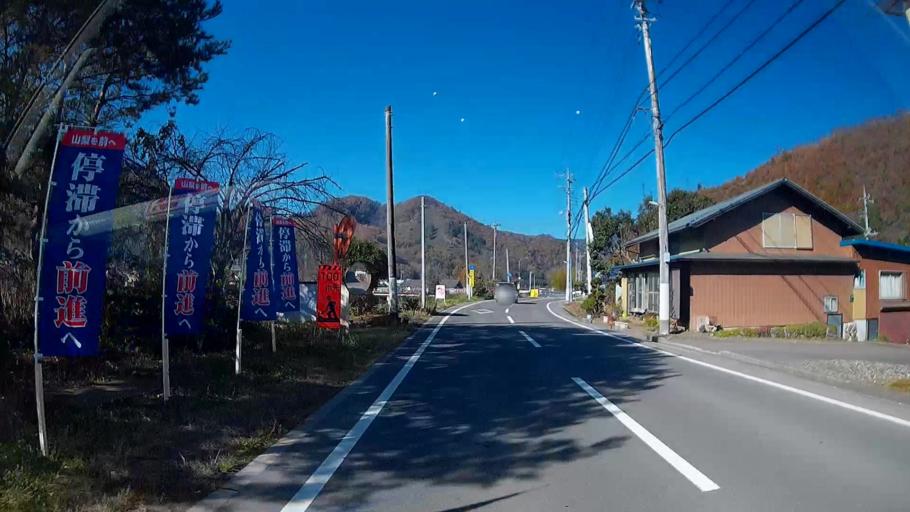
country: JP
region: Yamanashi
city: Otsuki
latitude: 35.5622
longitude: 138.9418
